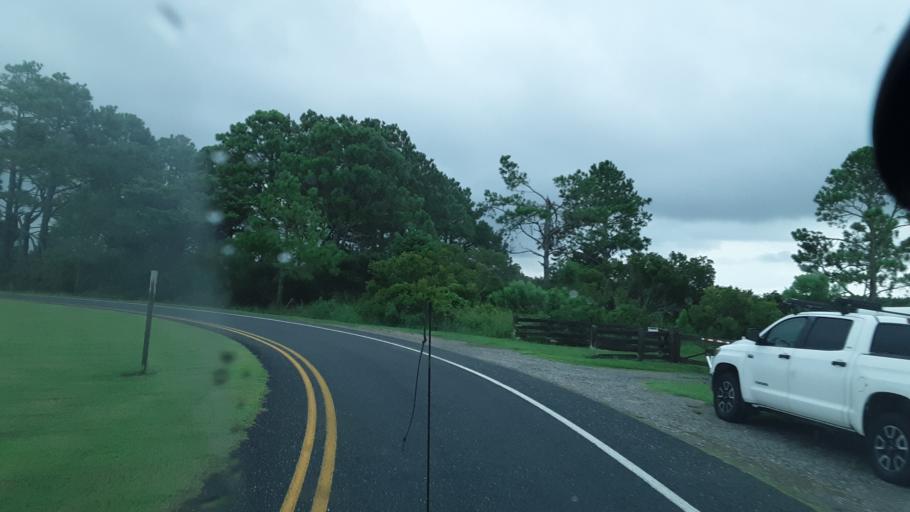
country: US
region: North Carolina
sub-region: Dare County
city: Wanchese
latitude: 35.8170
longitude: -75.5648
